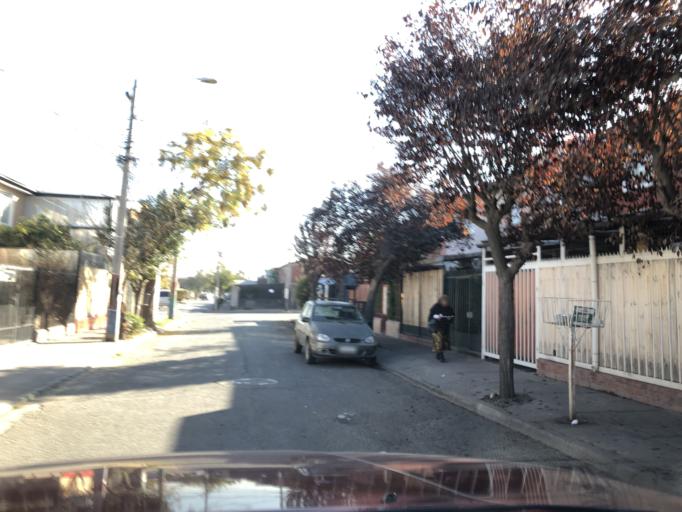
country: CL
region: Santiago Metropolitan
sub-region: Provincia de Cordillera
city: Puente Alto
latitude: -33.5997
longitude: -70.5642
